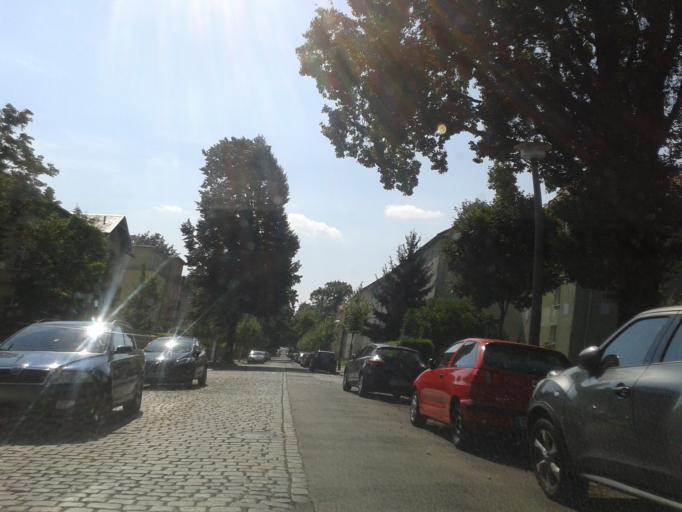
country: DE
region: Saxony
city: Dresden
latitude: 51.0381
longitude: 13.7287
